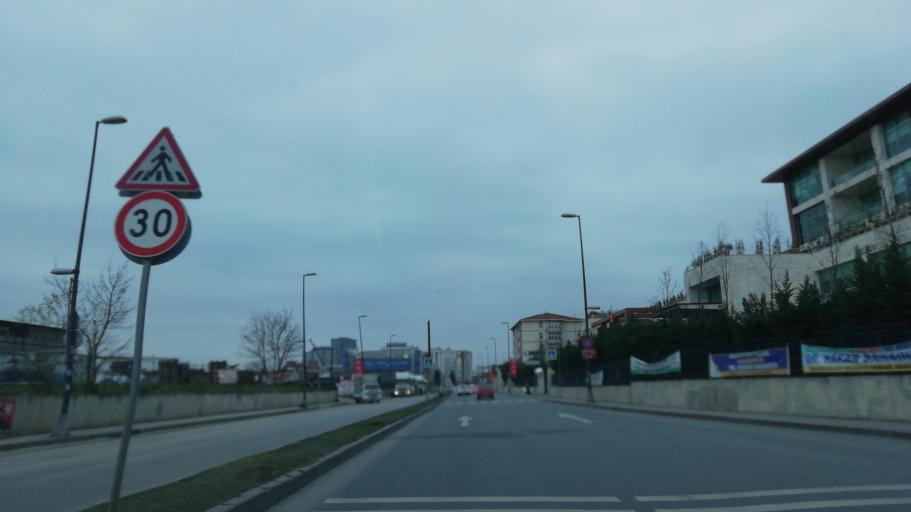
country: TR
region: Istanbul
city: Mahmutbey
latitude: 41.0127
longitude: 28.8182
